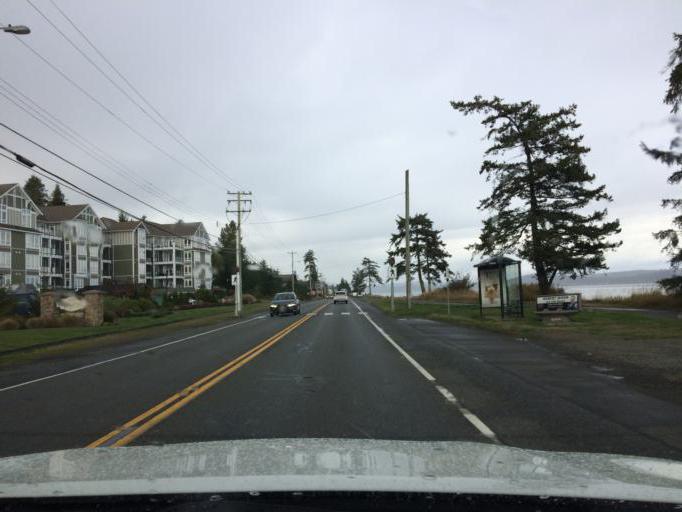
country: CA
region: British Columbia
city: Campbell River
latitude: 49.9962
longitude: -125.2298
